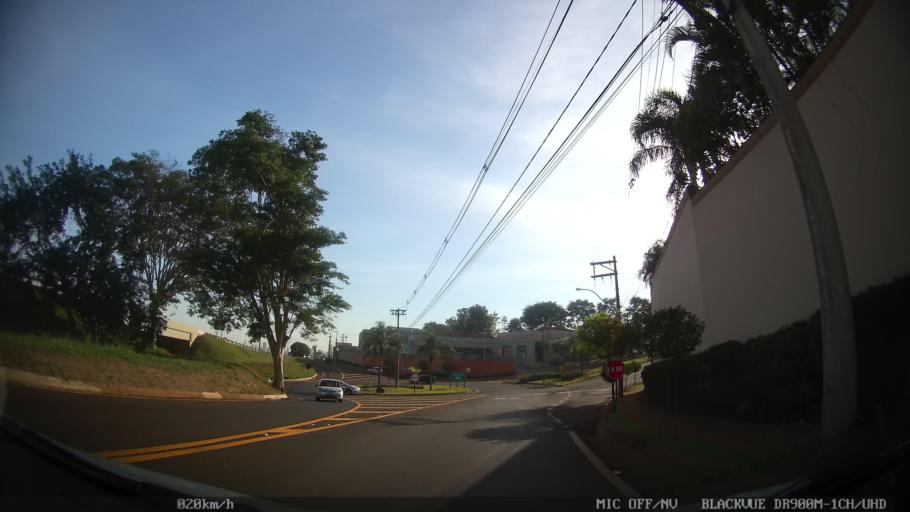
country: BR
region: Sao Paulo
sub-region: Ribeirao Preto
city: Ribeirao Preto
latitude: -21.2558
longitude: -47.8186
